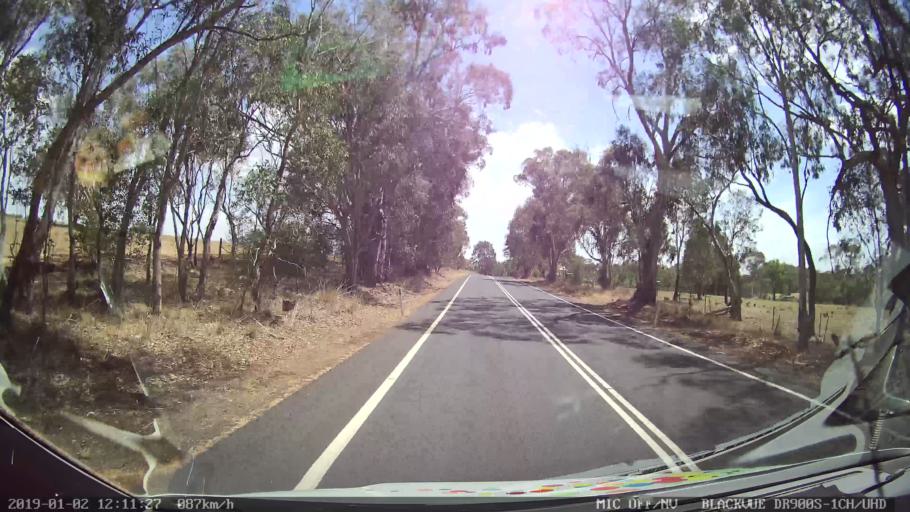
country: AU
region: New South Wales
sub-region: Young
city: Young
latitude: -34.4488
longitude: 148.2569
